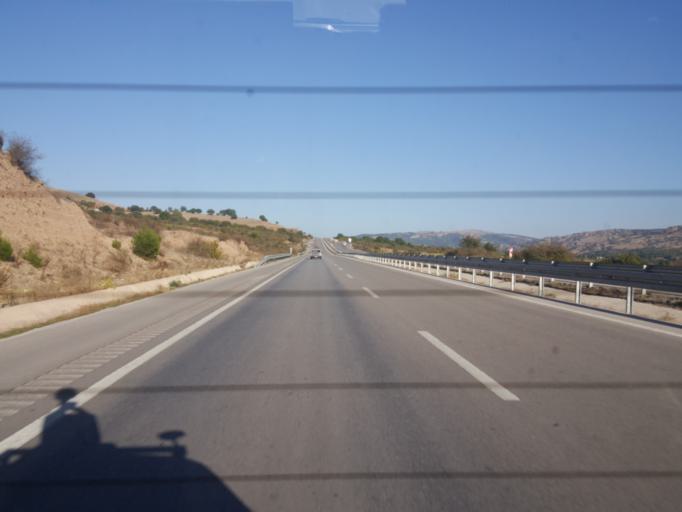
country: TR
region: Amasya
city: Tekke
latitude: 40.7396
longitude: 36.1968
